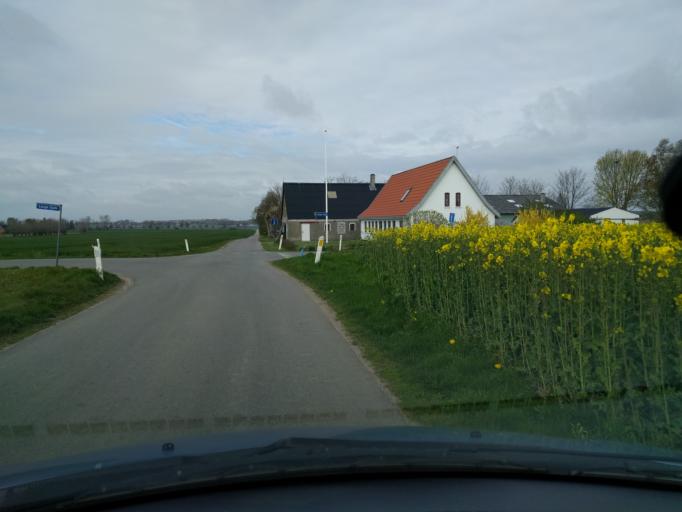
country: DK
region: South Denmark
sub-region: Kerteminde Kommune
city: Munkebo
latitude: 55.4457
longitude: 10.5901
